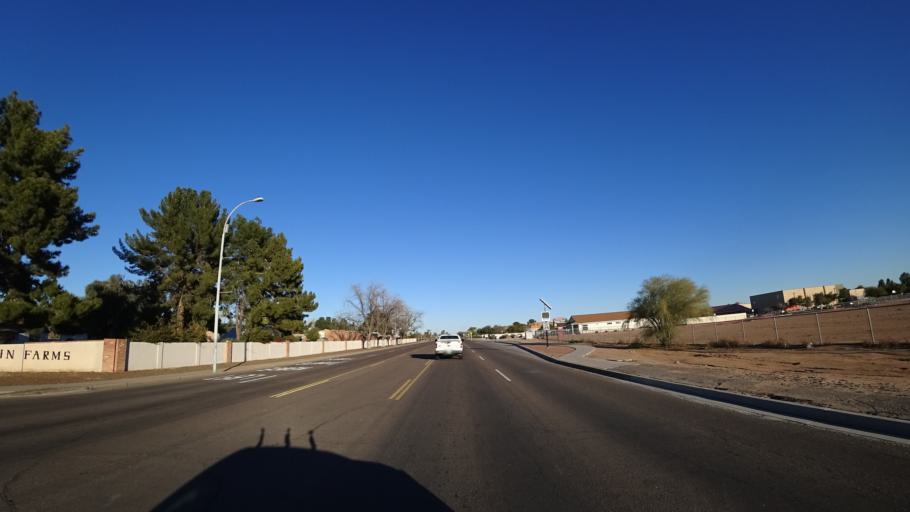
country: US
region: Arizona
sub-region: Maricopa County
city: Tolleson
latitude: 33.4505
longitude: -112.2531
